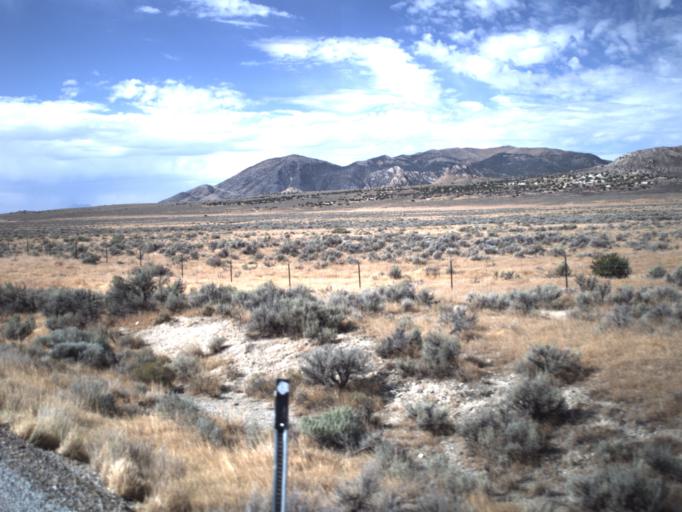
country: US
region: Utah
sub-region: Tooele County
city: Wendover
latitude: 41.5349
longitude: -113.5924
